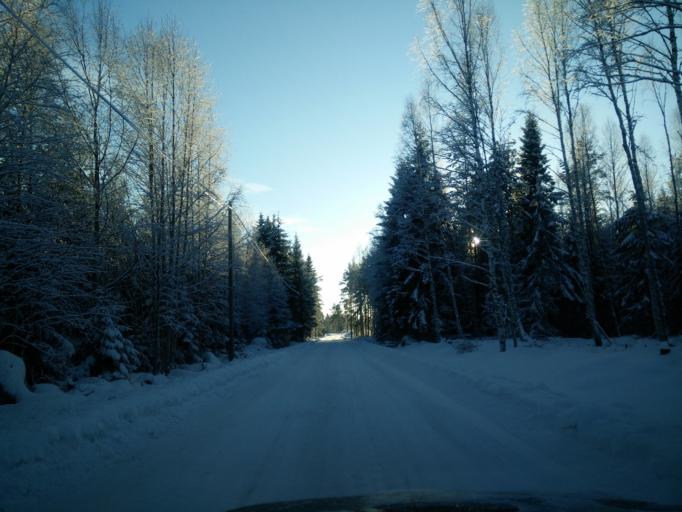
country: SE
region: Vaesternorrland
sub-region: Sundsvalls Kommun
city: Njurundabommen
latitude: 62.2128
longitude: 17.4937
